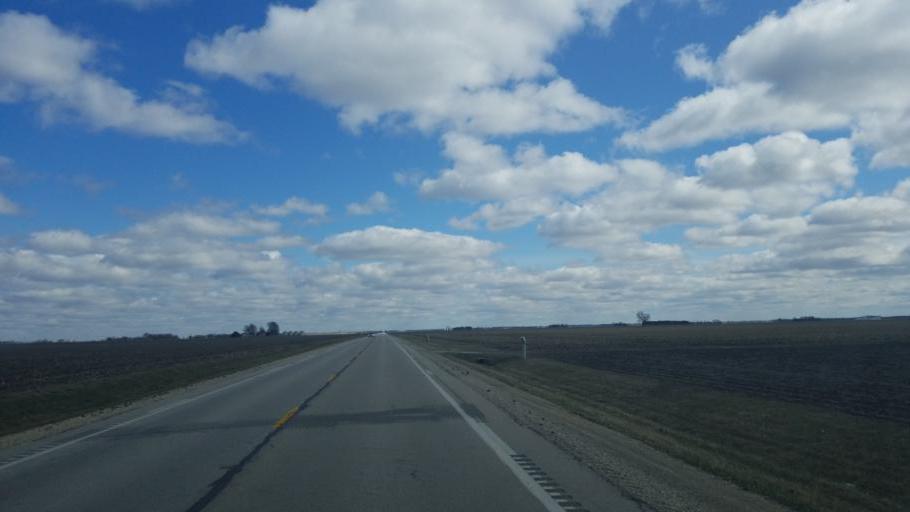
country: US
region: Illinois
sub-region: Douglas County
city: Villa Grove
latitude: 39.7919
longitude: -88.1349
